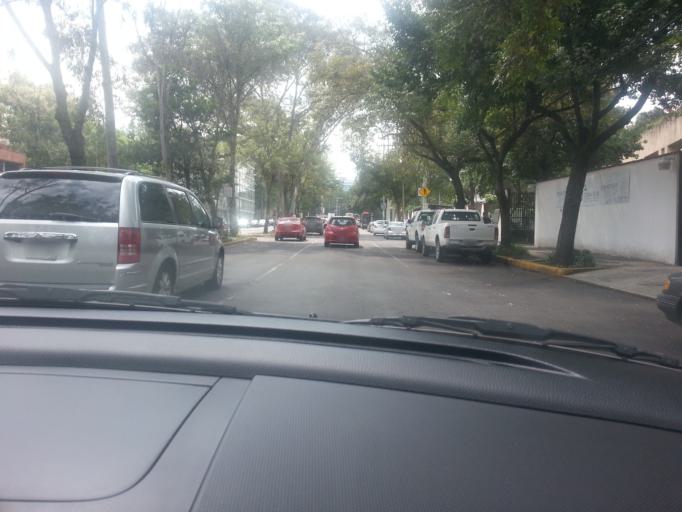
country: MX
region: Mexico City
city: Coyoacan
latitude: 19.3514
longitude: -99.1754
